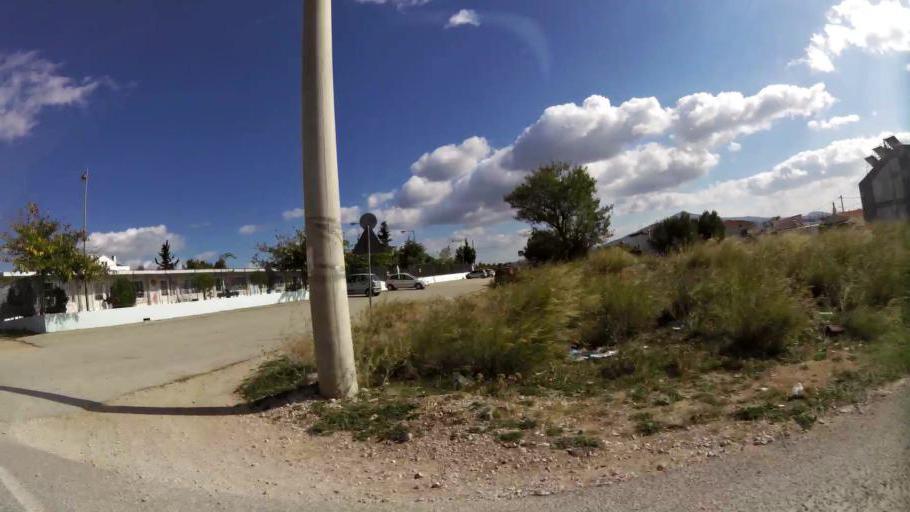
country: GR
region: Attica
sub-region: Nomarchia Anatolikis Attikis
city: Thrakomakedones
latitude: 38.1183
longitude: 23.7486
